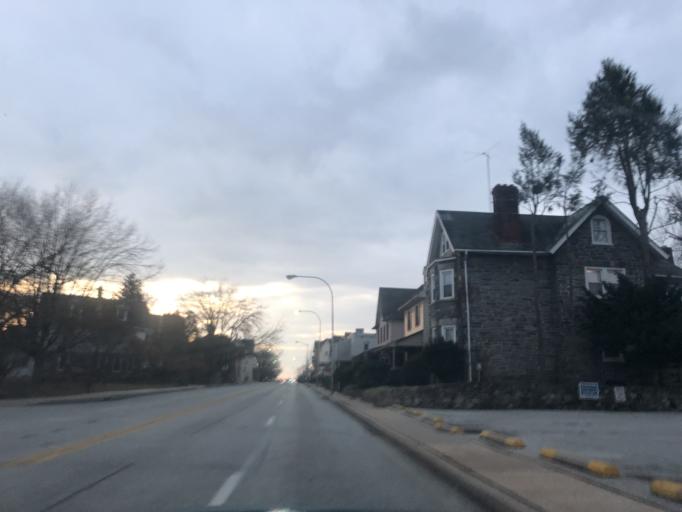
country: US
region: Pennsylvania
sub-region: Montgomery County
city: Bryn Mawr
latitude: 40.0216
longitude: -75.3250
